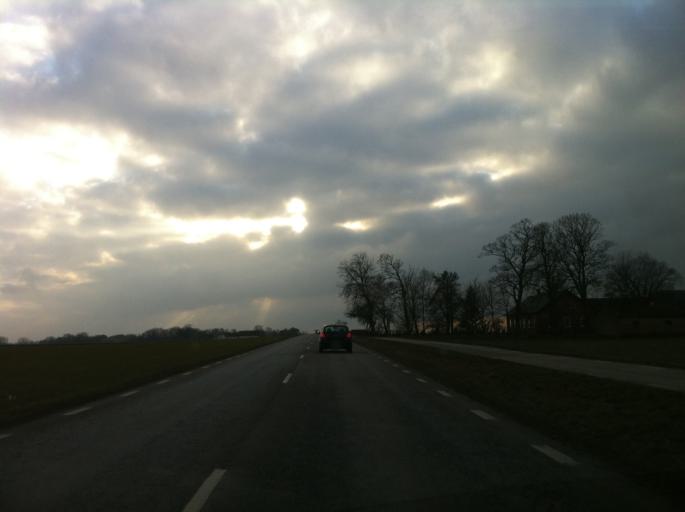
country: SE
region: Skane
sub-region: Kavlinge Kommun
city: Kaevlinge
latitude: 55.7878
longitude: 13.0856
